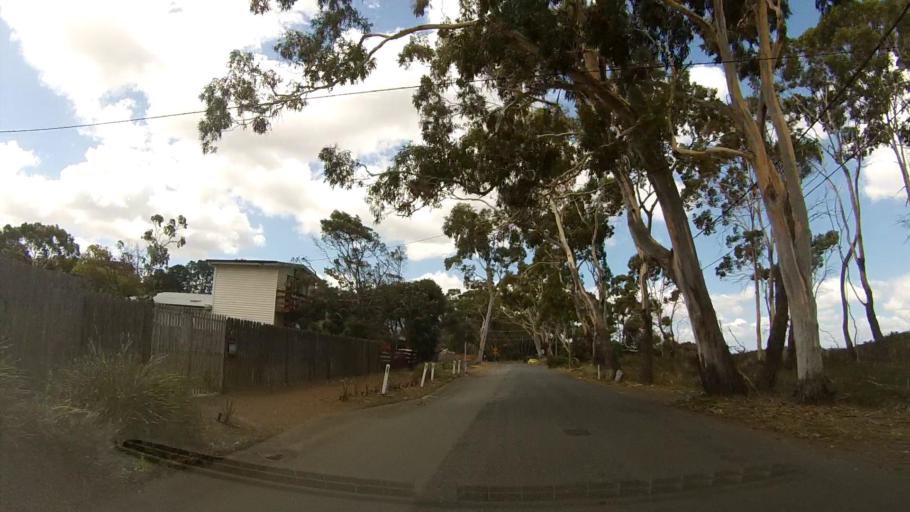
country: AU
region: Tasmania
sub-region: Clarence
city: Seven Mile Beach
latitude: -42.8633
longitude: 147.5048
